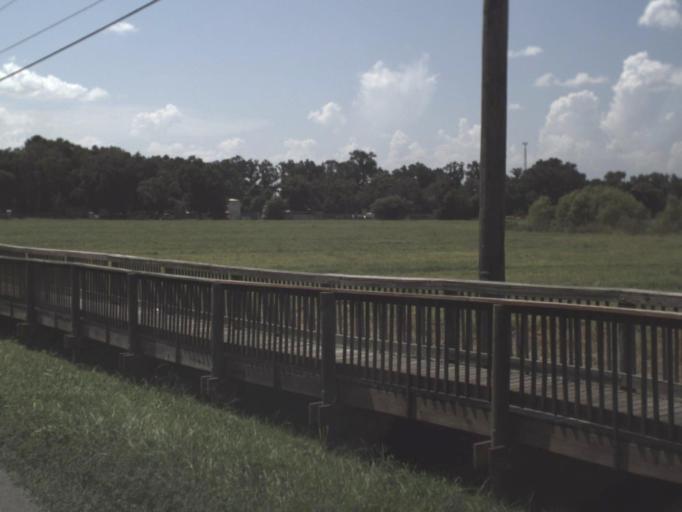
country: US
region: Florida
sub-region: Hillsborough County
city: Dover
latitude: 28.0206
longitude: -82.2248
